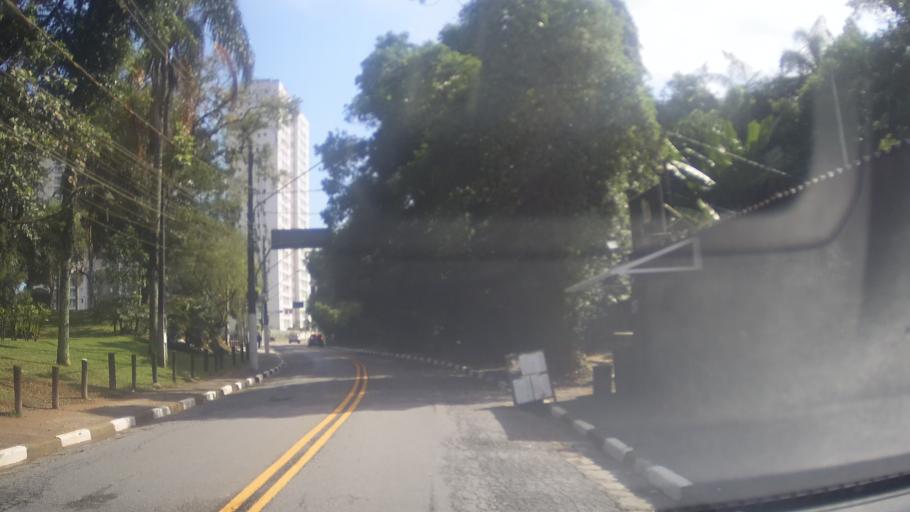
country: BR
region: Sao Paulo
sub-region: Santos
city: Santos
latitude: -23.9472
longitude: -46.3543
